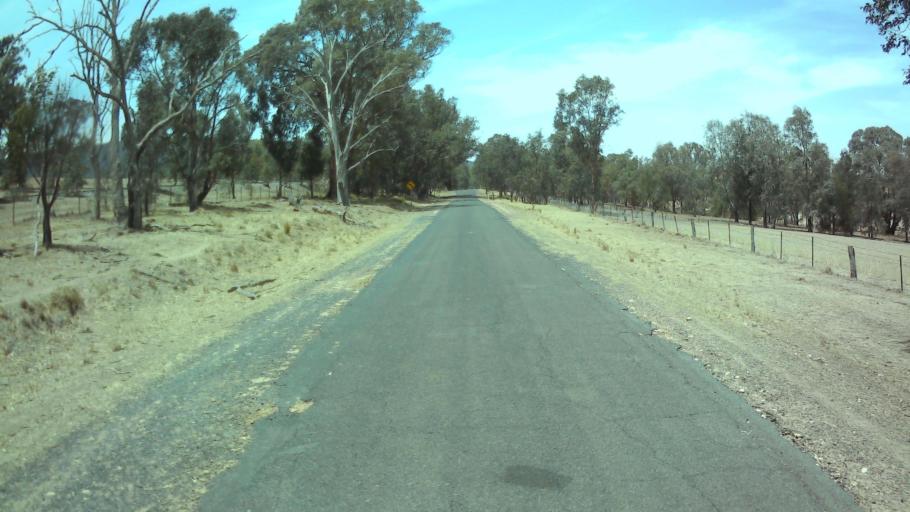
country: AU
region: New South Wales
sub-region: Weddin
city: Grenfell
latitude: -34.0251
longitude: 148.4318
